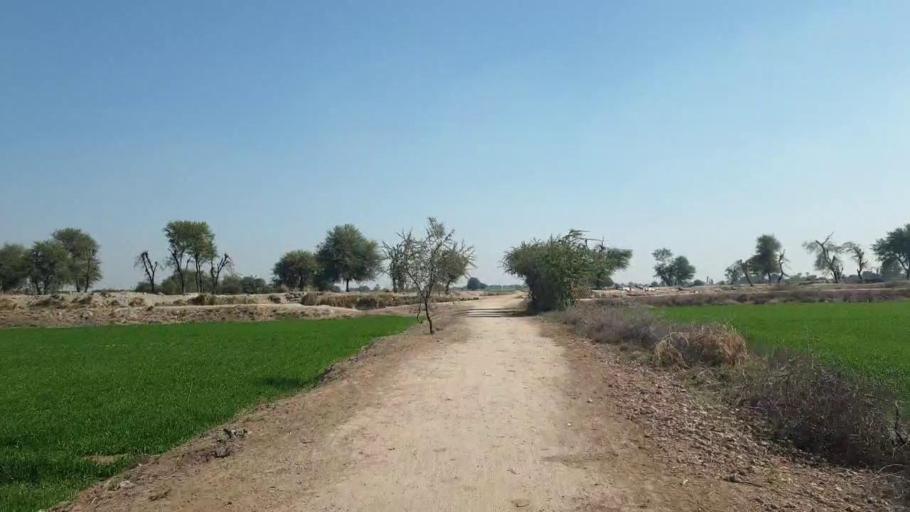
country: PK
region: Sindh
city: Shahpur Chakar
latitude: 26.1245
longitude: 68.6477
